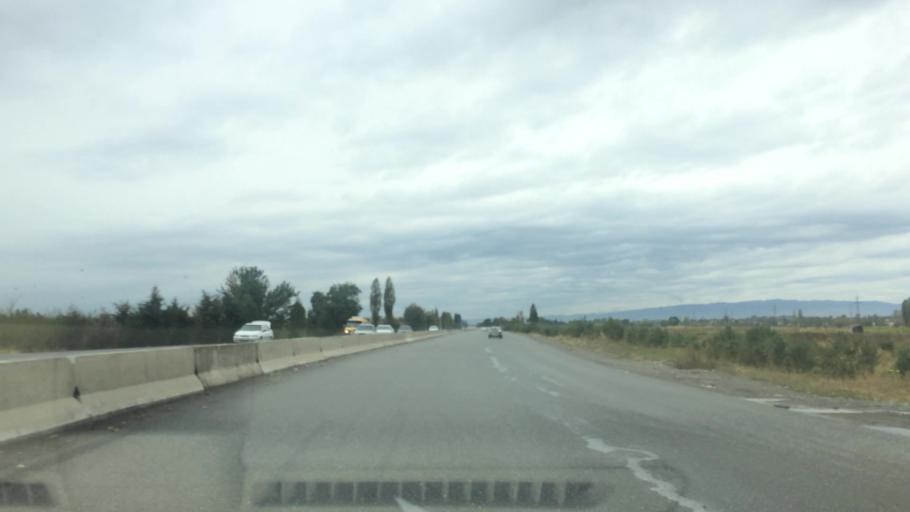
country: UZ
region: Jizzax
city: Jizzax
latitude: 40.0210
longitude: 67.6130
